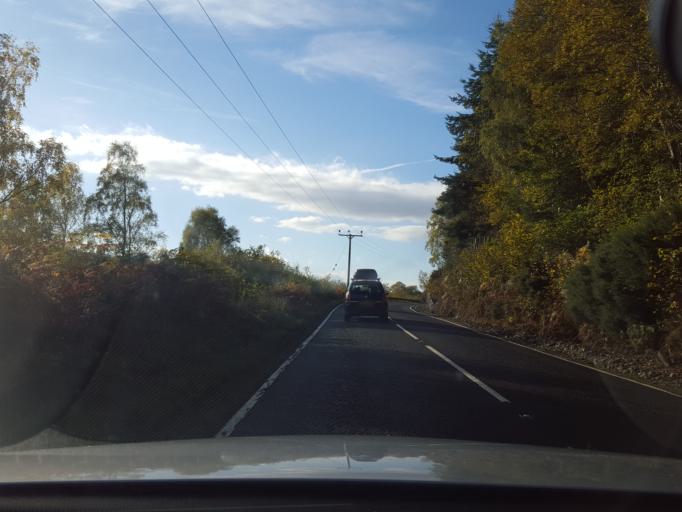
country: GB
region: Scotland
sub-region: Highland
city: Beauly
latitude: 57.2341
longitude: -4.5609
